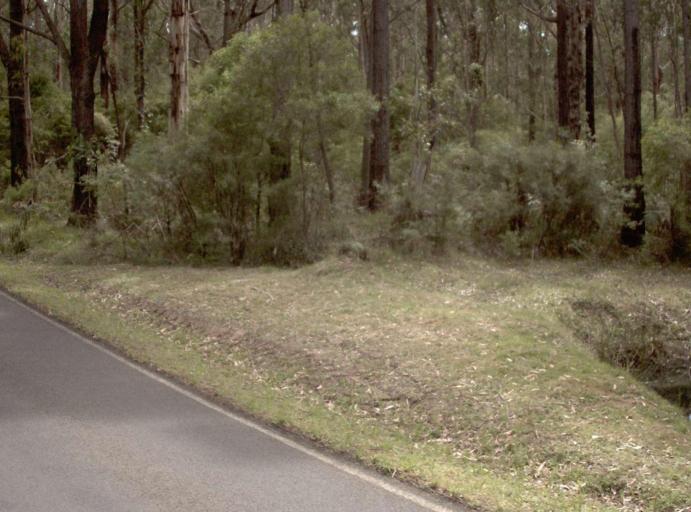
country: AU
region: Victoria
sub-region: Latrobe
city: Morwell
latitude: -38.0371
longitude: 146.4190
